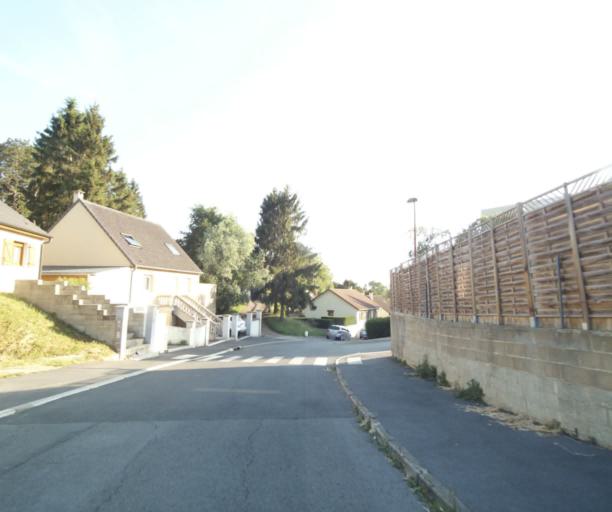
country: FR
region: Champagne-Ardenne
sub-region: Departement des Ardennes
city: Charleville-Mezieres
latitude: 49.7852
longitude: 4.7158
